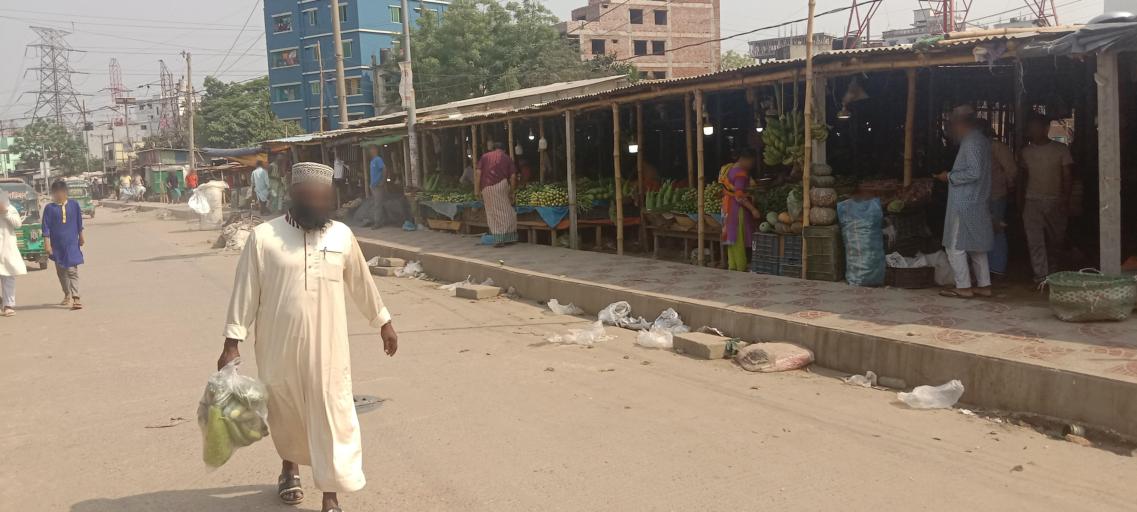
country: BD
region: Dhaka
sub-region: Dhaka
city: Dhaka
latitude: 23.6818
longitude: 90.4249
